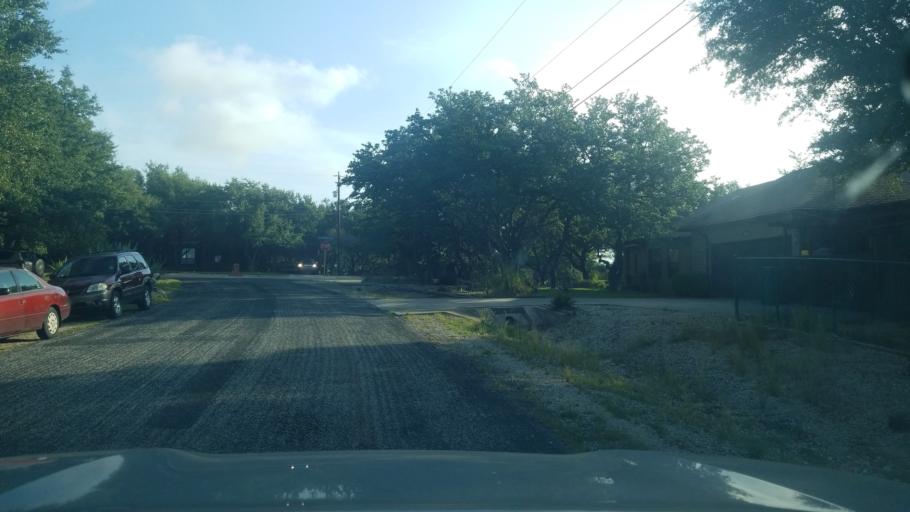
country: US
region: Texas
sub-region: Bexar County
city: Timberwood Park
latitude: 29.7012
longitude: -98.5092
